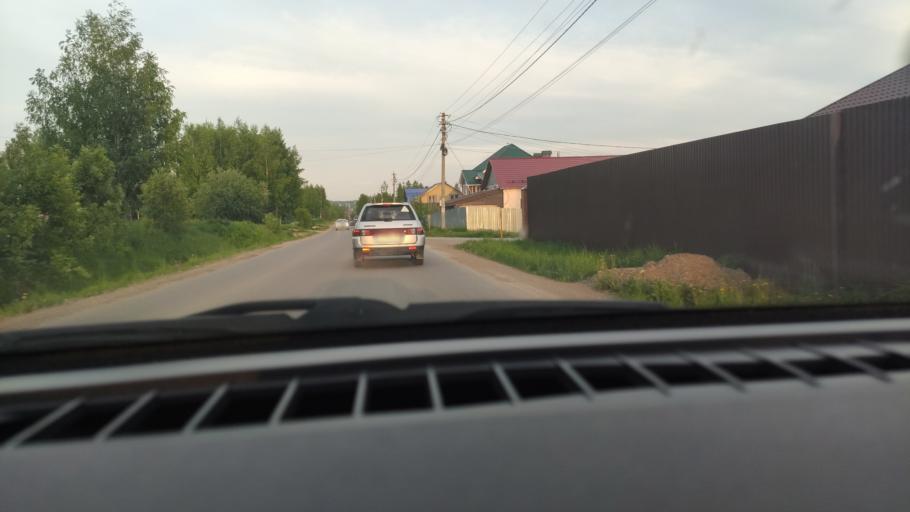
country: RU
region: Perm
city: Kondratovo
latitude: 58.0578
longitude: 56.0072
